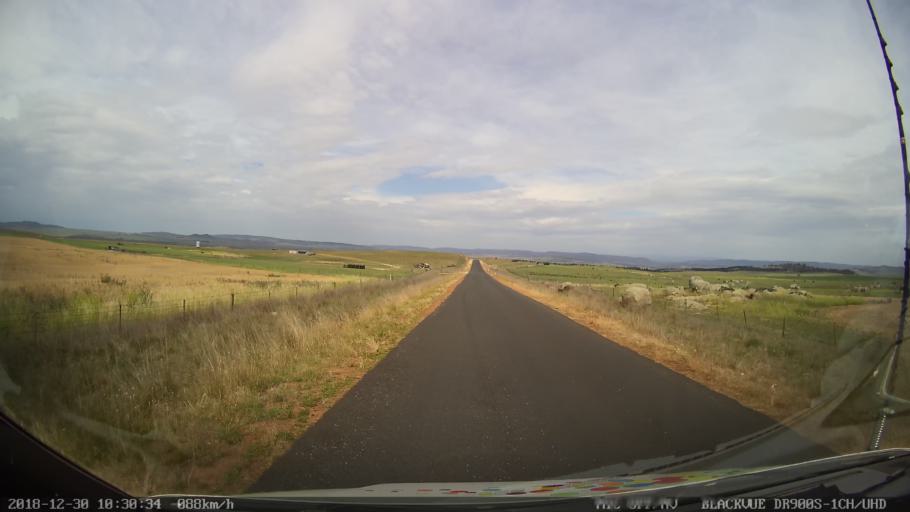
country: AU
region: New South Wales
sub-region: Snowy River
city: Berridale
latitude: -36.5041
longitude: 148.8931
